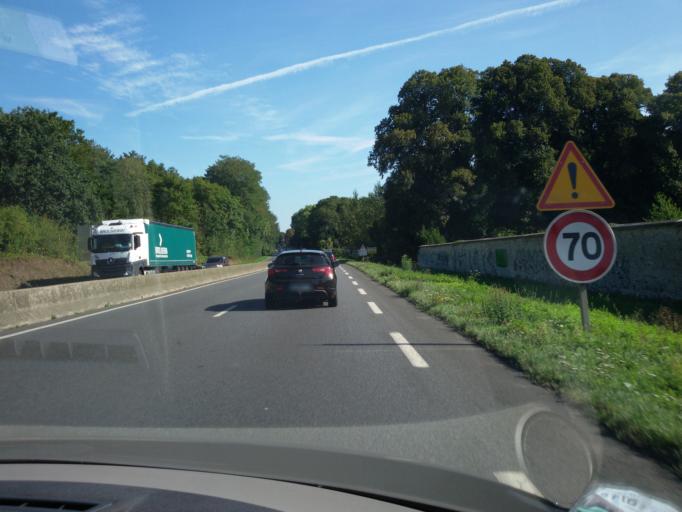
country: FR
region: Ile-de-France
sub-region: Departement de l'Essonne
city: Etrechy
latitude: 48.4738
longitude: 2.1882
